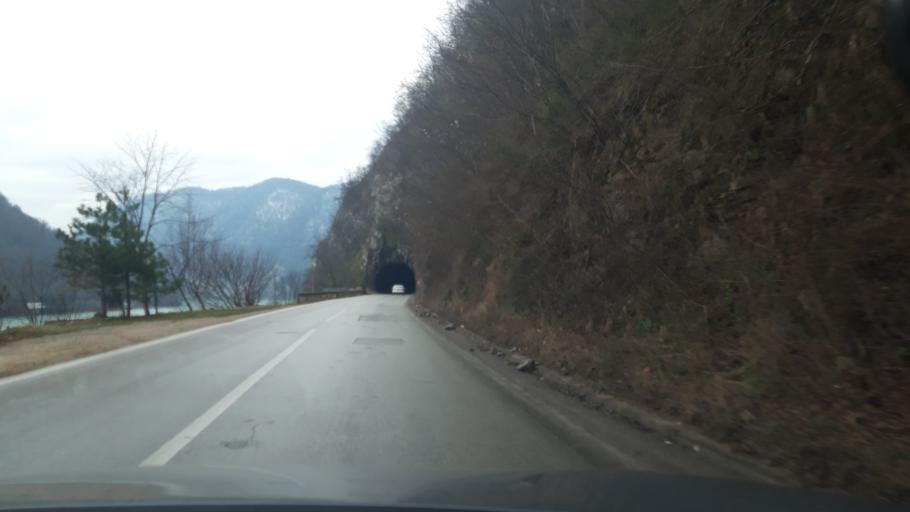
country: RS
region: Central Serbia
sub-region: Macvanski Okrug
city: Mali Zvornik
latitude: 44.3481
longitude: 19.1111
